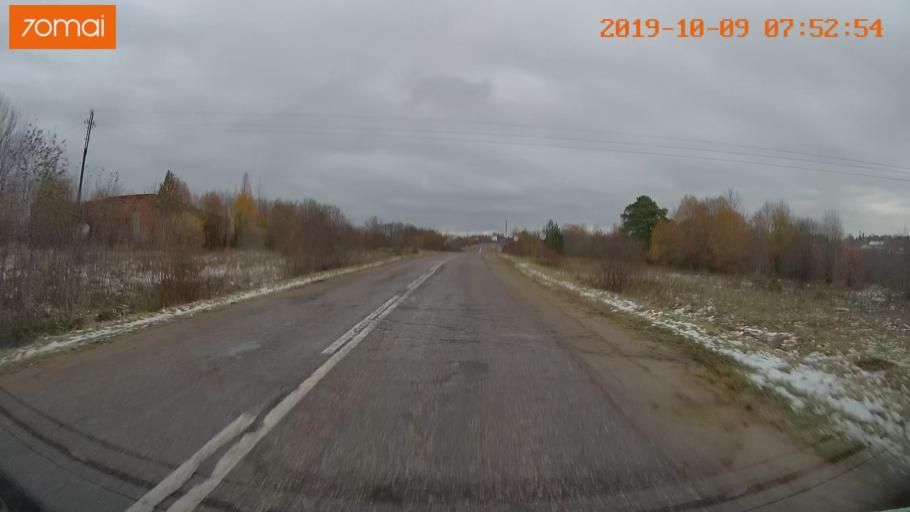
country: RU
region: Jaroslavl
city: Kukoboy
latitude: 58.6947
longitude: 39.8905
